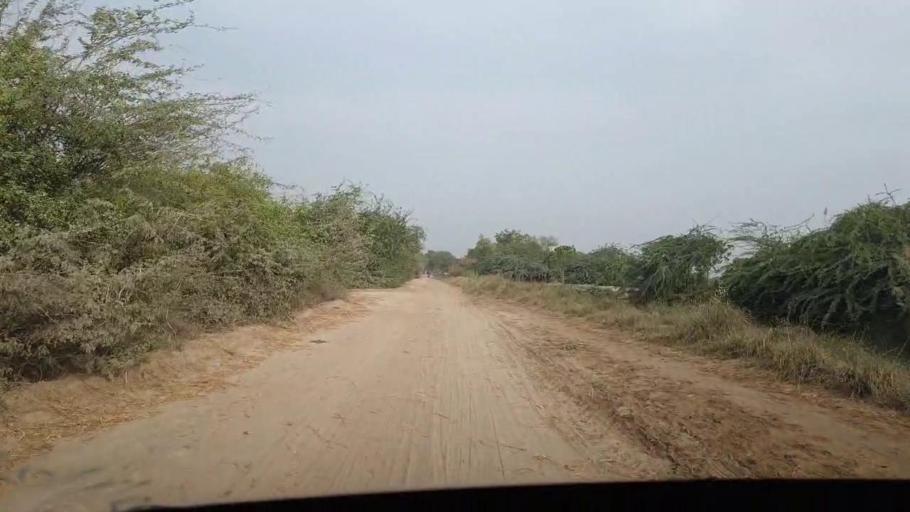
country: PK
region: Sindh
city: Chuhar Jamali
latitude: 24.3947
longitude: 67.9737
